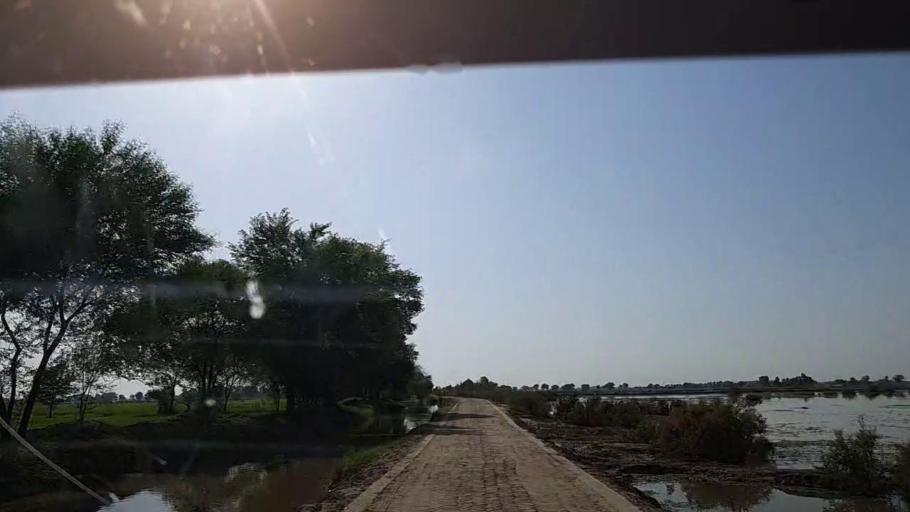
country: PK
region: Sindh
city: Tangwani
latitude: 28.2152
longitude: 68.9728
